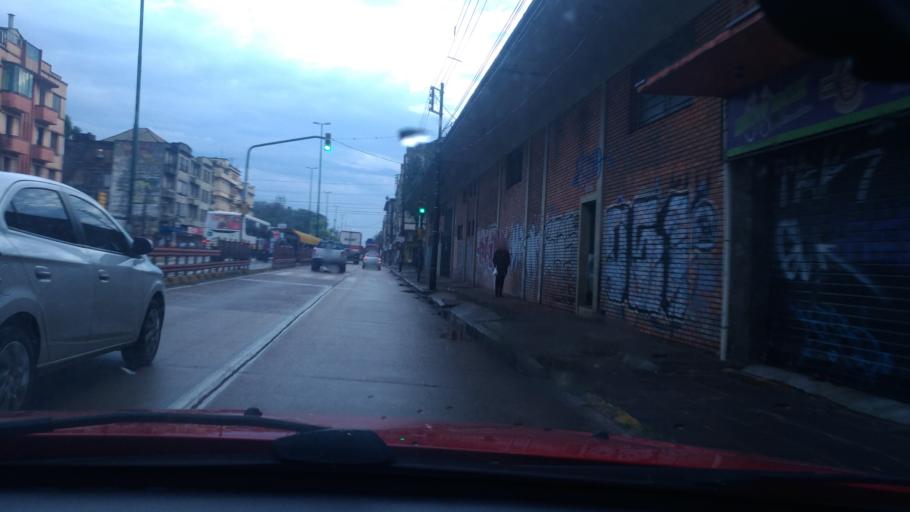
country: BR
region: Rio Grande do Sul
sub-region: Porto Alegre
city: Porto Alegre
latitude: -30.0078
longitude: -51.2015
